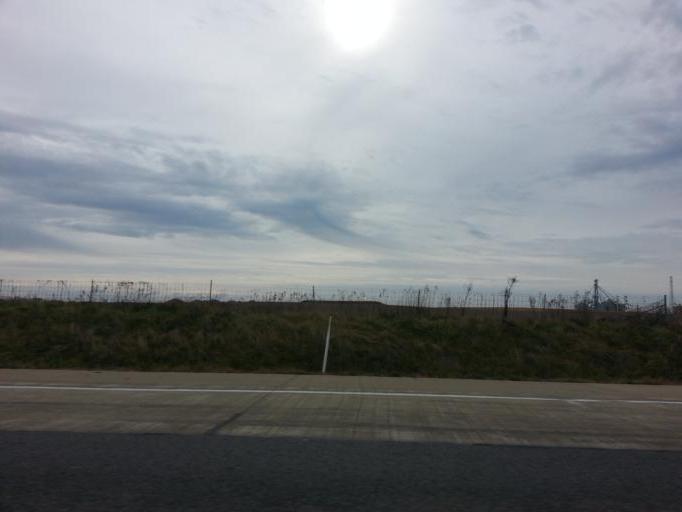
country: US
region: Indiana
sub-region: Decatur County
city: Greensburg
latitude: 39.3621
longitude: -85.5058
